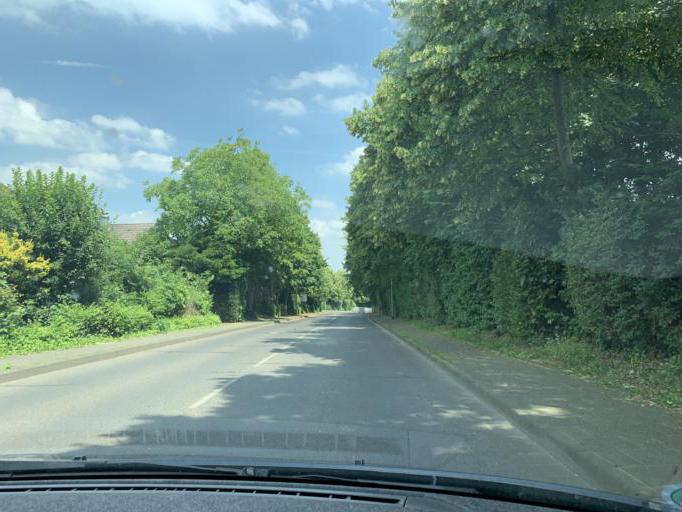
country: DE
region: North Rhine-Westphalia
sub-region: Regierungsbezirk Koln
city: Bedburg
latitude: 50.9905
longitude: 6.5665
